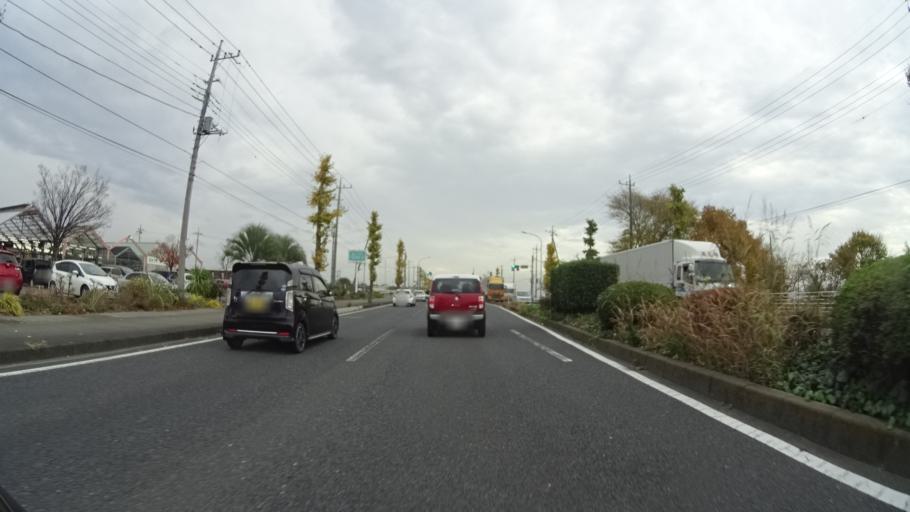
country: JP
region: Gunma
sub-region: Sawa-gun
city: Tamamura
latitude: 36.3701
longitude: 139.1438
